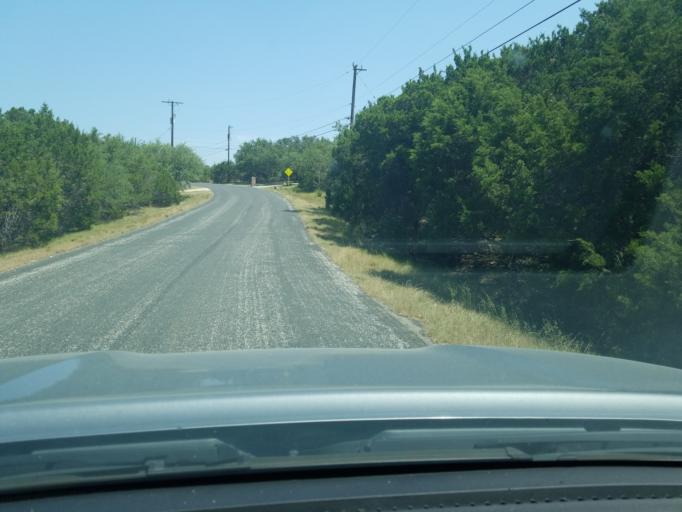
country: US
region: Texas
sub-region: Bexar County
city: Timberwood Park
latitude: 29.6964
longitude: -98.4844
